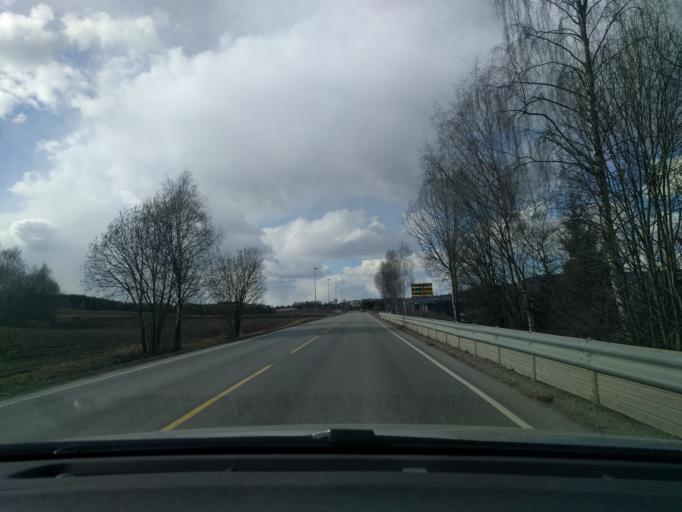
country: NO
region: Hedmark
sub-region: Hamar
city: Hamar
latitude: 60.8369
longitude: 11.0538
